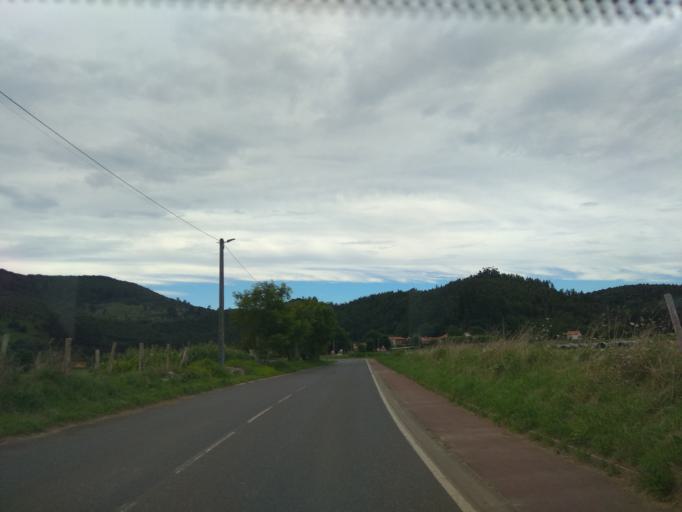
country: ES
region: Cantabria
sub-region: Provincia de Cantabria
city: Hazas de Cesto
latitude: 43.3971
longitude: -3.5946
